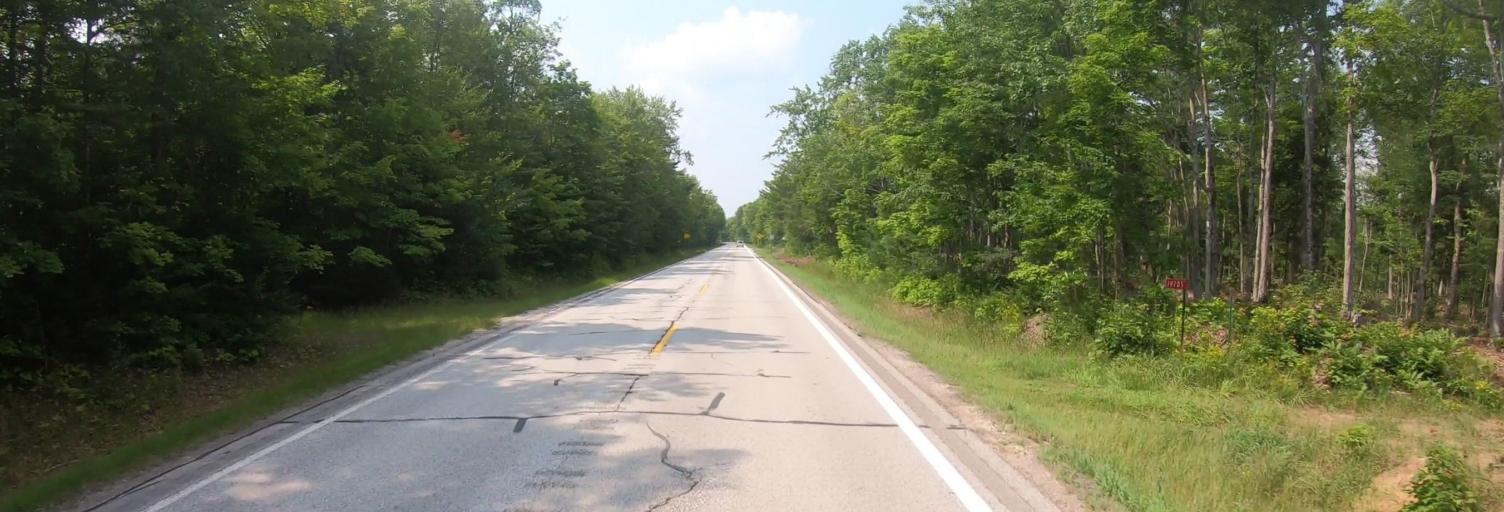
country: US
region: Michigan
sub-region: Luce County
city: Newberry
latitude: 46.5178
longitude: -85.4198
